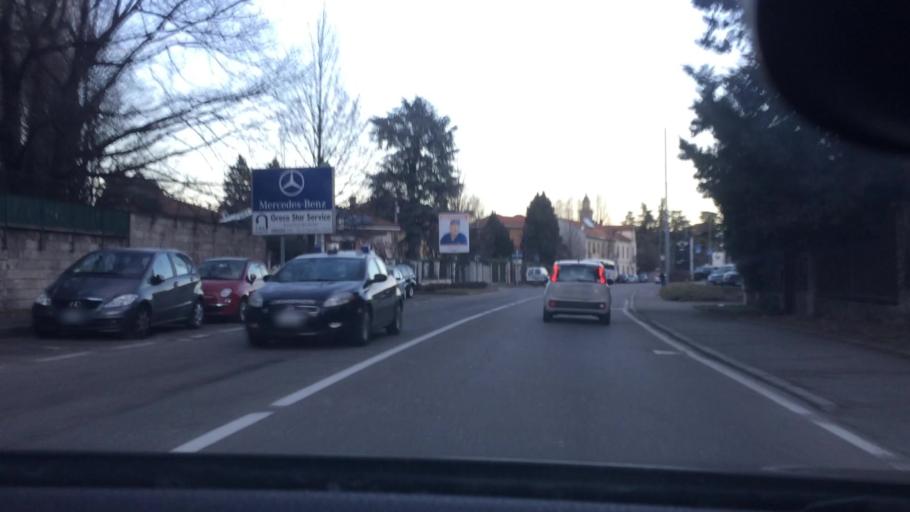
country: IT
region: Lombardy
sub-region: Provincia di Varese
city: Saronno
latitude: 45.6238
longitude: 9.0210
